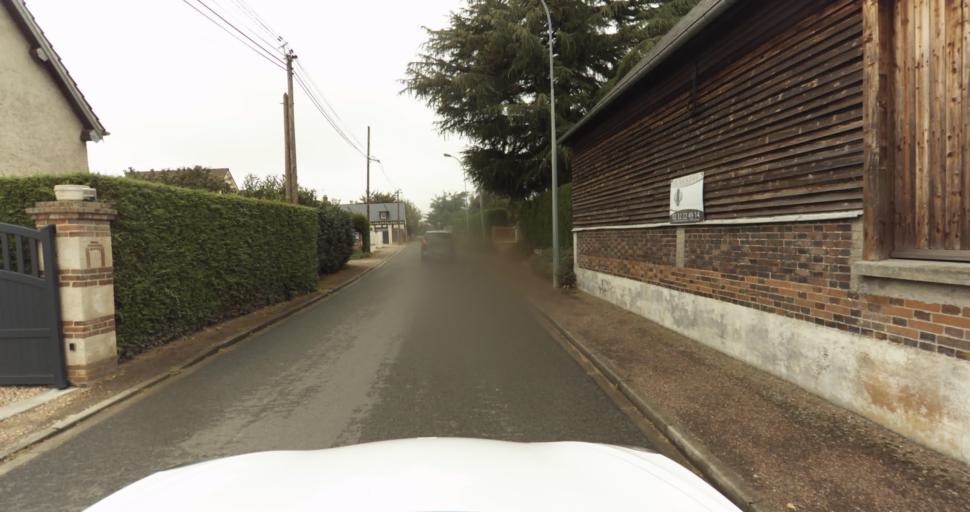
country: FR
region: Haute-Normandie
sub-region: Departement de l'Eure
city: Aviron
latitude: 49.0802
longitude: 1.0777
